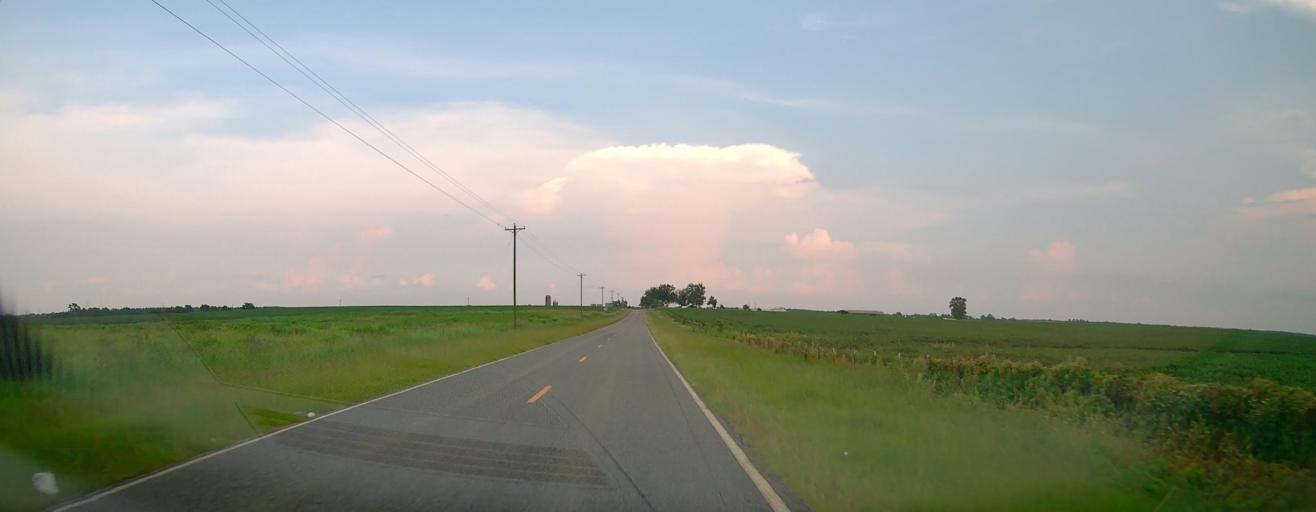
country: US
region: Georgia
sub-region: Laurens County
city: East Dublin
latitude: 32.6463
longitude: -82.8214
